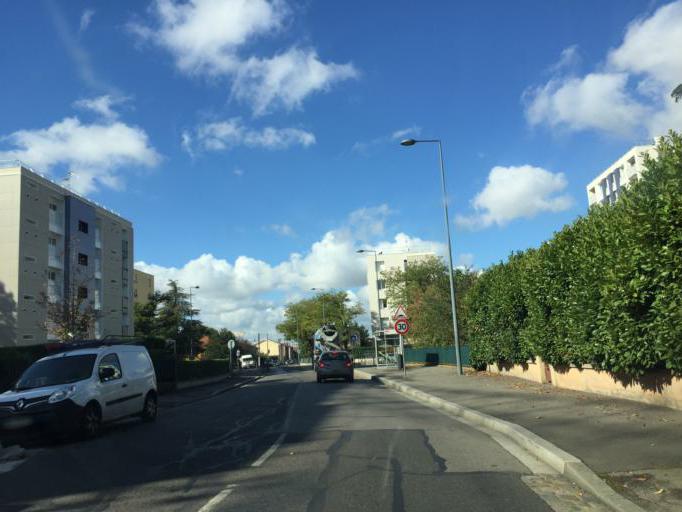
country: FR
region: Rhone-Alpes
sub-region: Departement du Rhone
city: Bron
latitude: 45.7547
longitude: 4.9175
